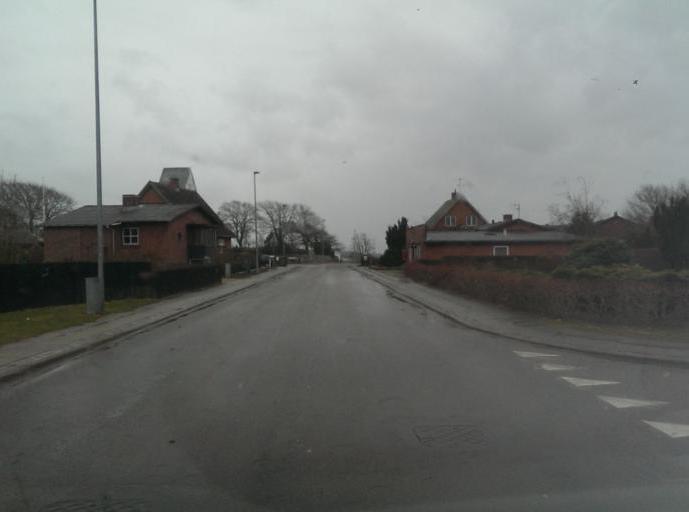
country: DK
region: Central Jutland
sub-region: Ringkobing-Skjern Kommune
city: Skjern
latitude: 56.0010
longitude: 8.4184
